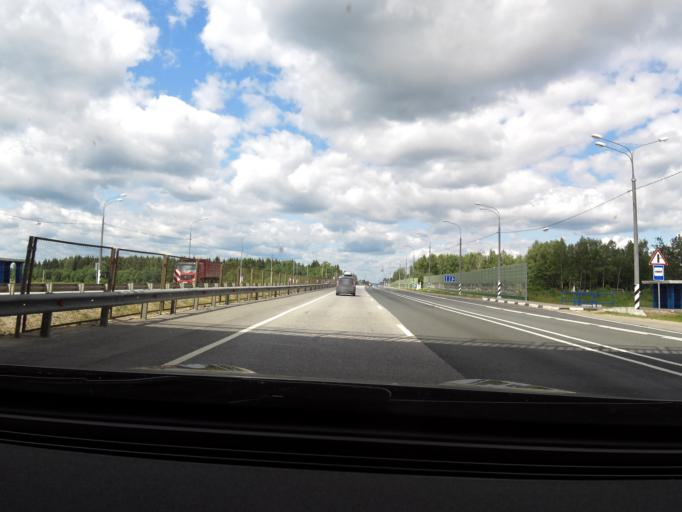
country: RU
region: Tverskaya
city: Torzhok
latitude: 56.9984
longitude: 35.1623
